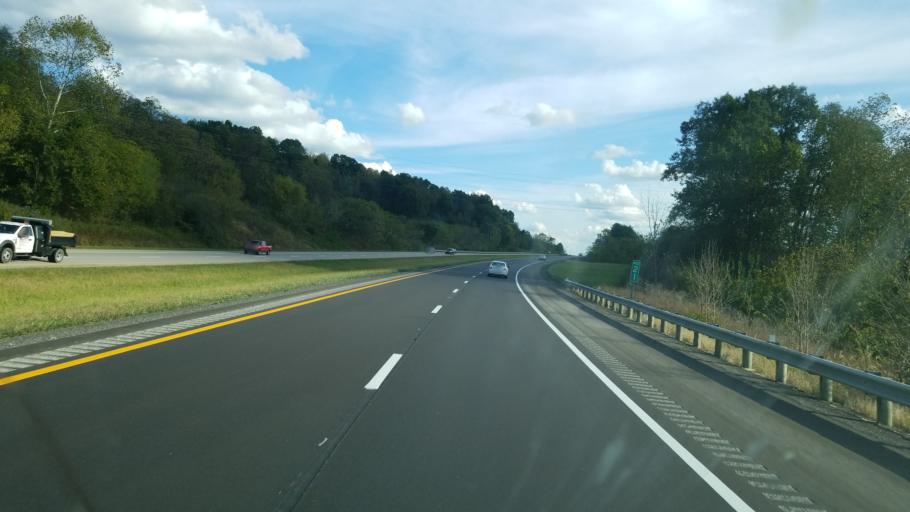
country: US
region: Ohio
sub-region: Noble County
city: Caldwell
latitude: 39.6872
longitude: -81.4956
